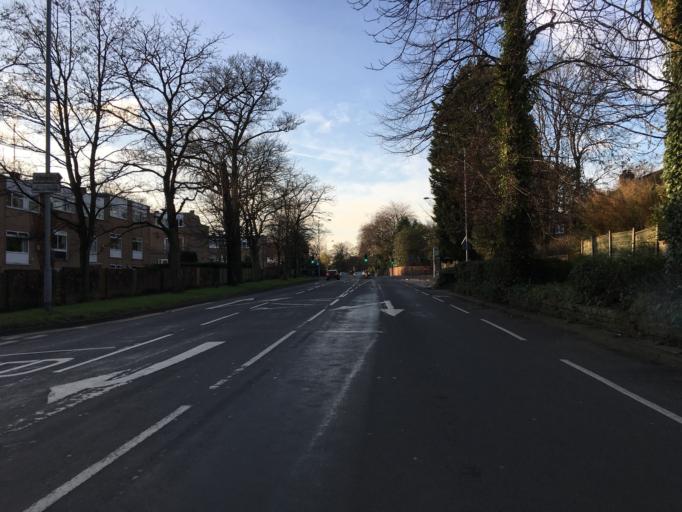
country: GB
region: England
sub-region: Borough of Stockport
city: Cheadle Heath
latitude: 53.4136
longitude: -2.1969
